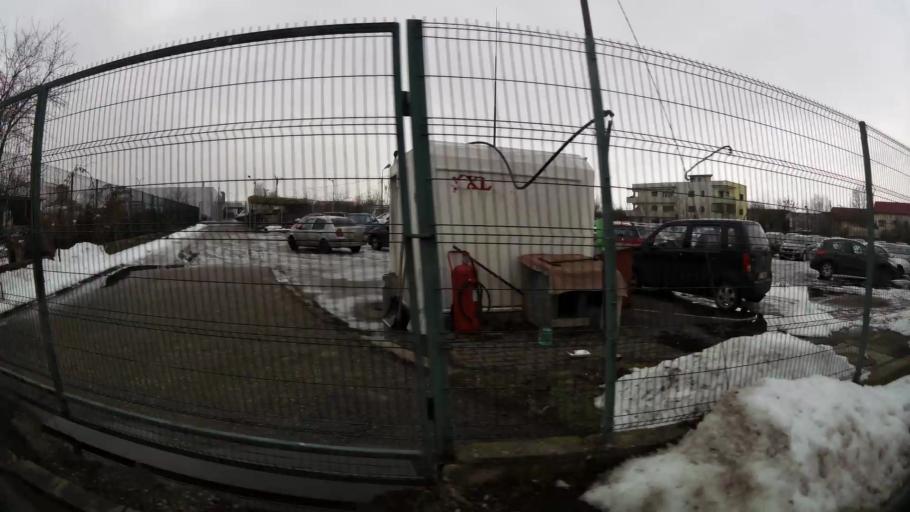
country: RO
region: Ilfov
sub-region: Comuna Otopeni
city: Otopeni
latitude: 44.5430
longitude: 26.0713
